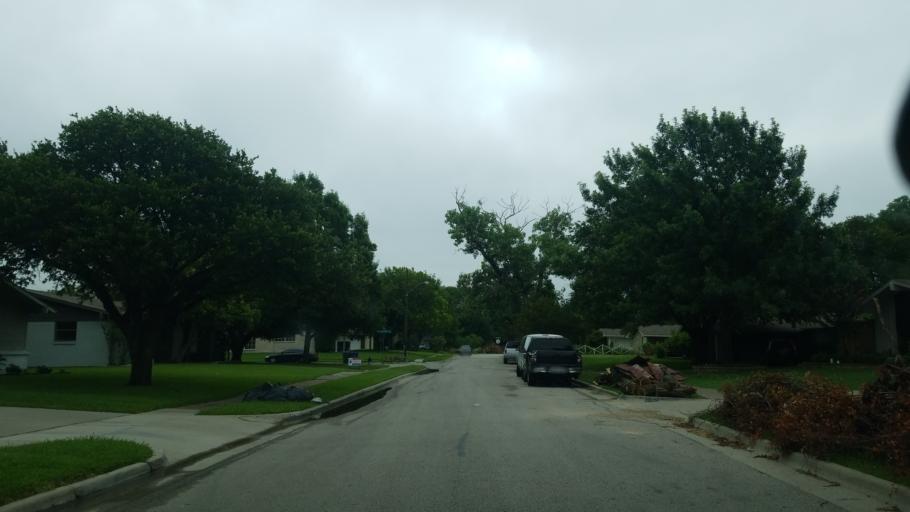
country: US
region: Texas
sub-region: Dallas County
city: Farmers Branch
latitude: 32.9076
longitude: -96.8683
